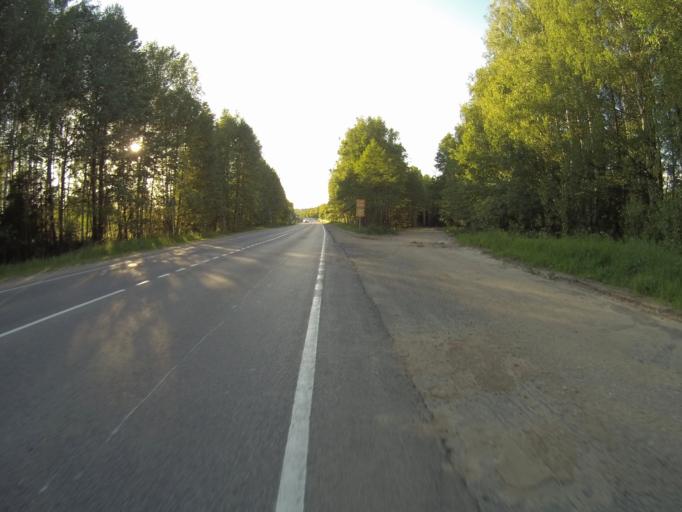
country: RU
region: Vladimir
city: Golovino
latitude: 55.9454
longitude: 40.5831
